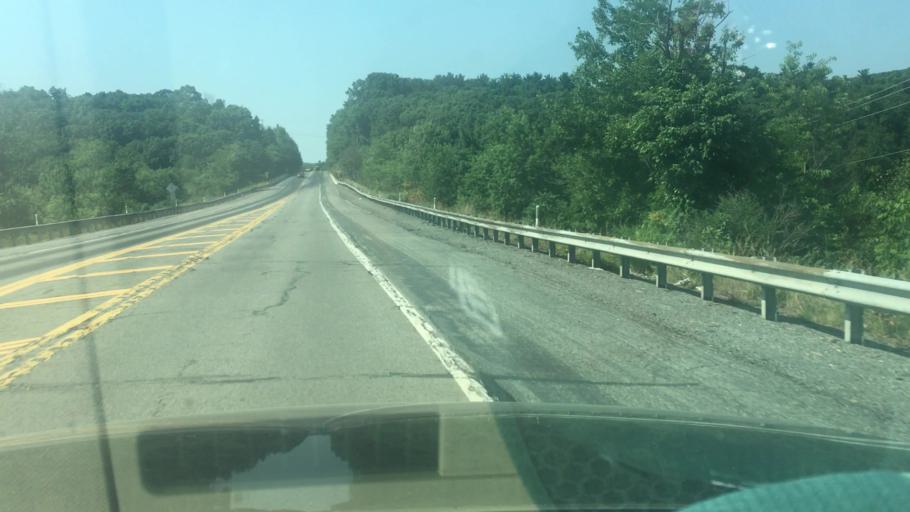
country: US
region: Pennsylvania
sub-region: Schuylkill County
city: Ashland
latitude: 40.7486
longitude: -76.3856
